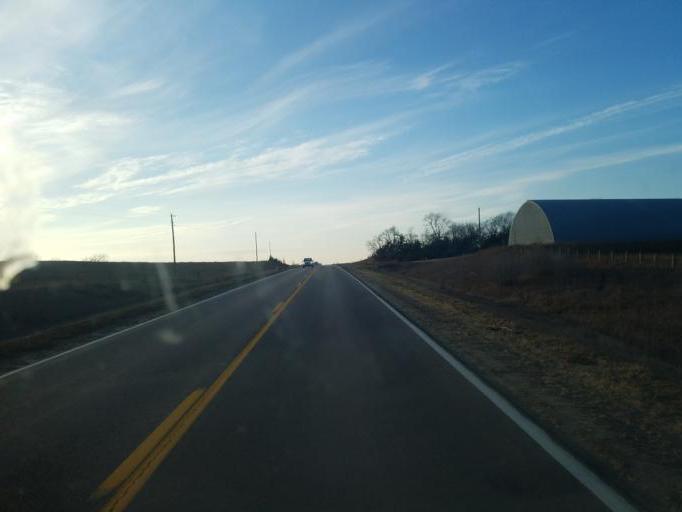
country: US
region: Nebraska
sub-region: Cedar County
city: Hartington
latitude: 42.7290
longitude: -97.3545
